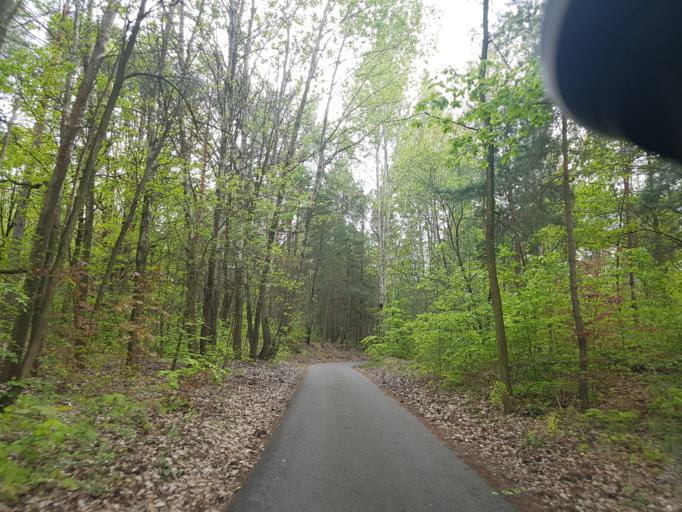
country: DE
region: Brandenburg
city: Tschernitz
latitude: 51.6106
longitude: 14.5852
